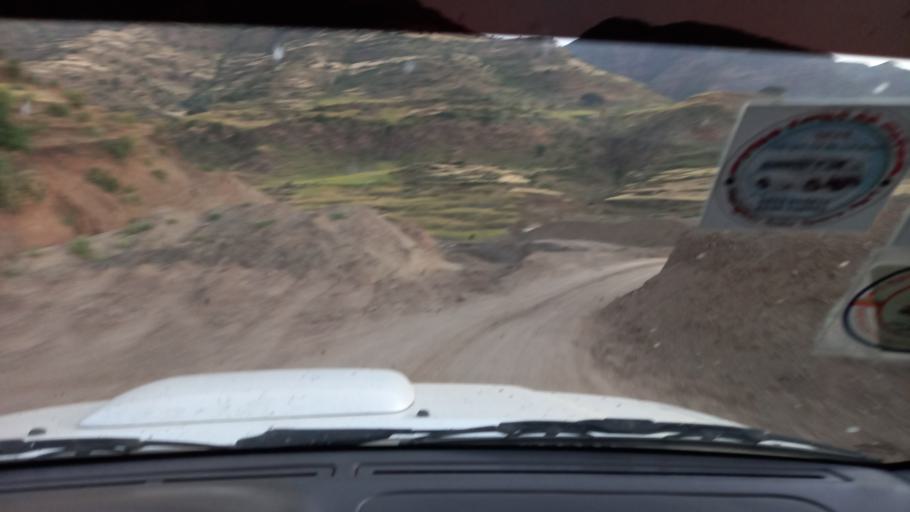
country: ET
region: Amhara
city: Debark'
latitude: 13.0320
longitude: 38.0538
